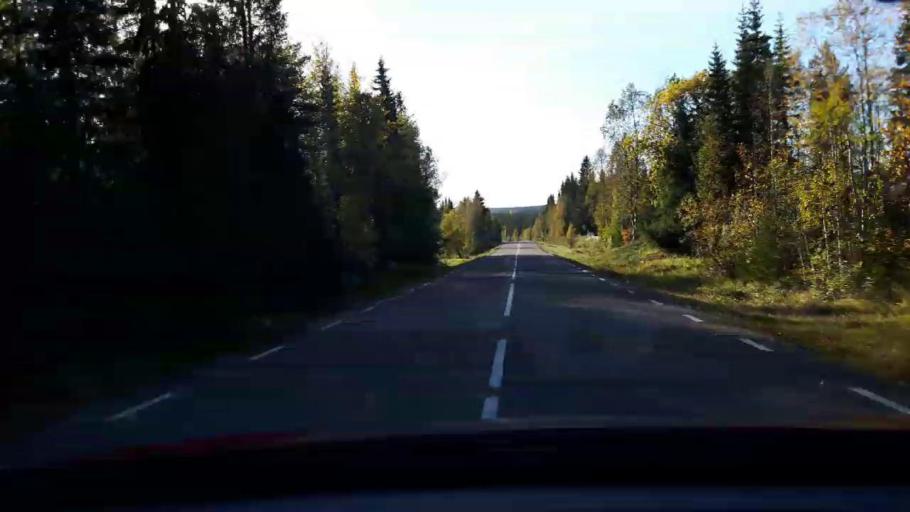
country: SE
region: Jaemtland
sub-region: Stroemsunds Kommun
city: Stroemsund
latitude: 63.8671
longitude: 15.1139
